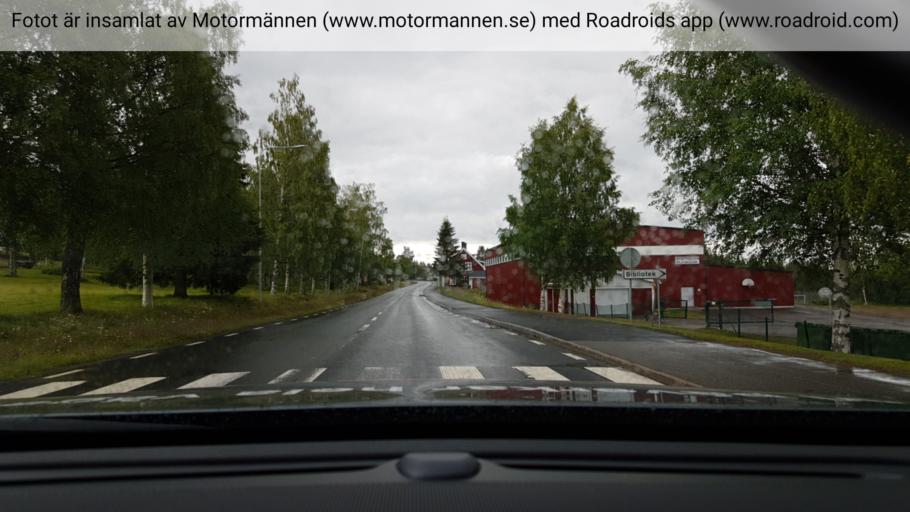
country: SE
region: Vaesterbotten
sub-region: Norsjo Kommun
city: Norsjoe
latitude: 65.2610
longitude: 19.6378
